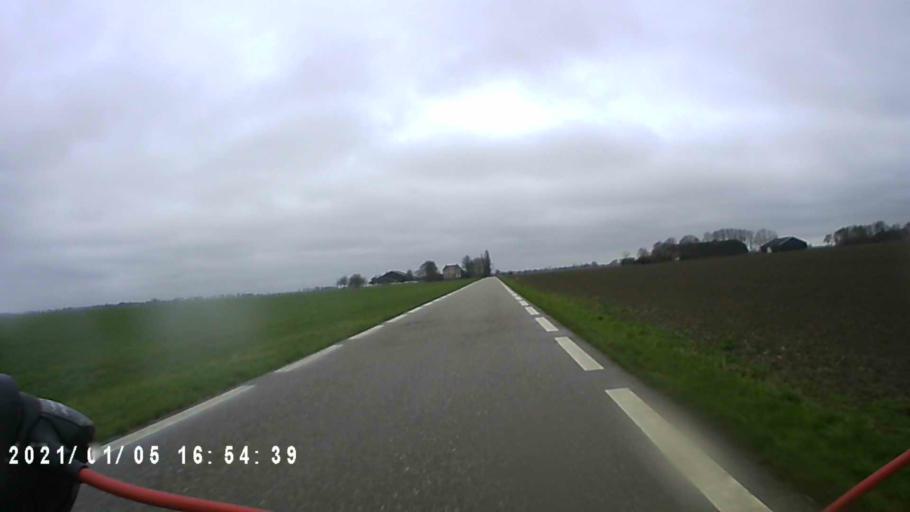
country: NL
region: Groningen
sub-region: Gemeente  Oldambt
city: Winschoten
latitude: 53.2416
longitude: 7.0566
